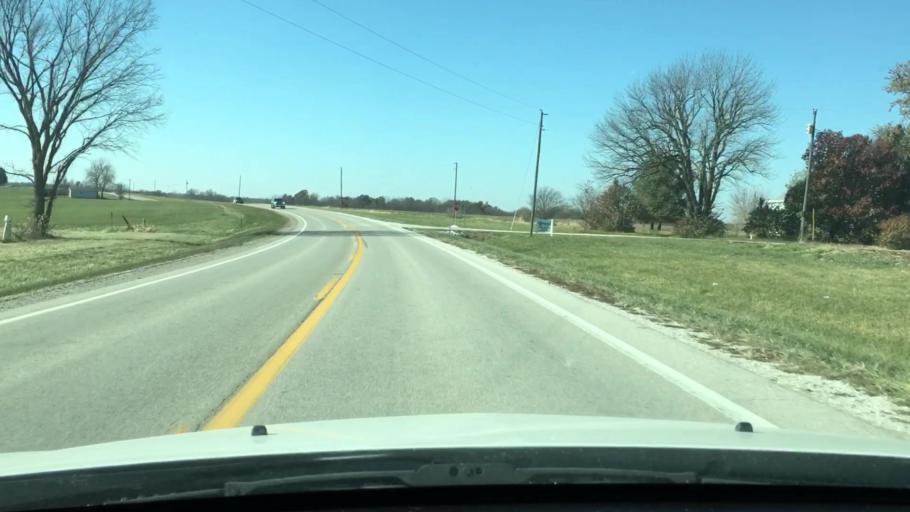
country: US
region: Illinois
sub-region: Pike County
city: Pittsfield
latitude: 39.6194
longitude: -90.7221
